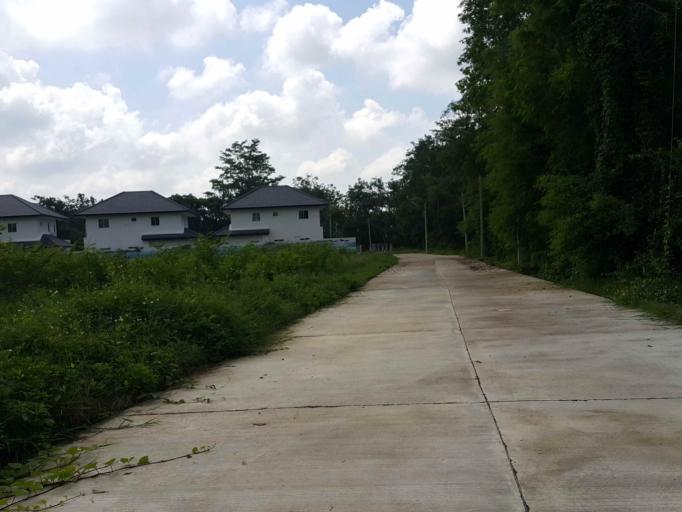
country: TH
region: Chiang Mai
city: San Kamphaeng
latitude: 18.7609
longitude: 99.1014
